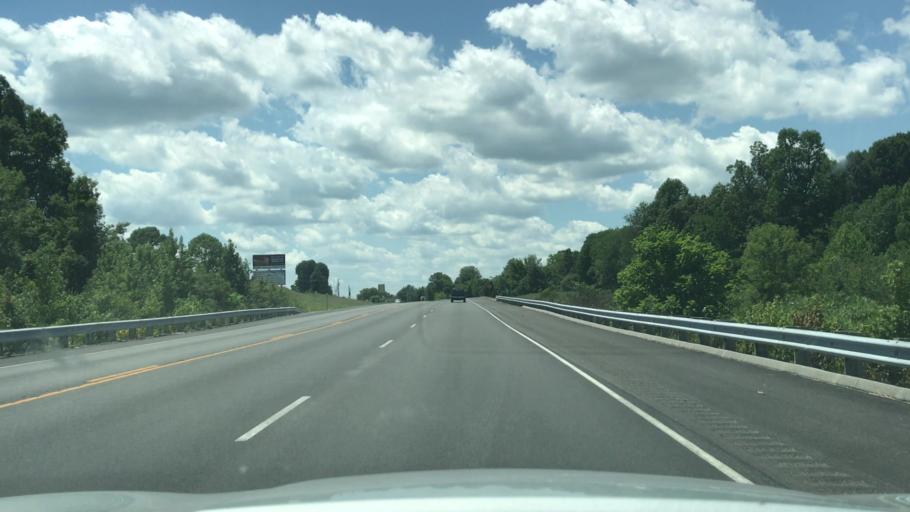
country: US
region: Kentucky
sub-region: Muhlenberg County
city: Greenville
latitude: 37.2026
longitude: -87.2008
